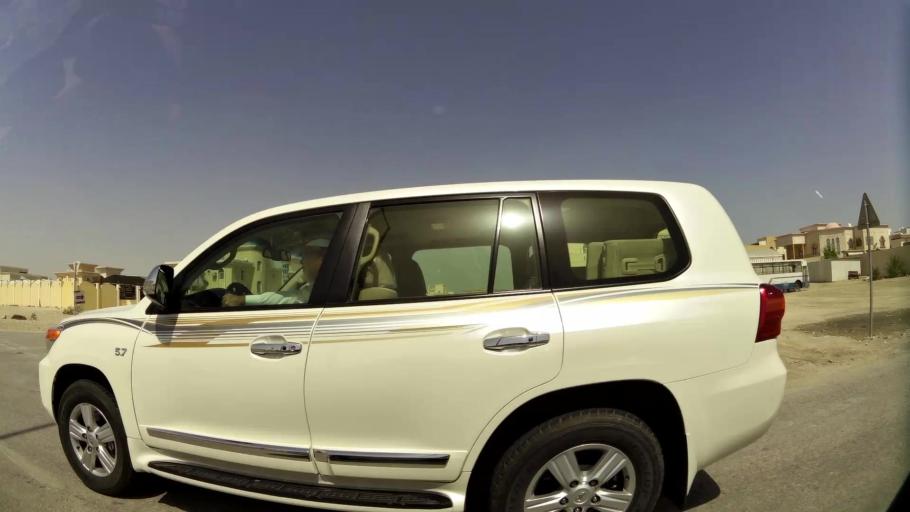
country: QA
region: Baladiyat Umm Salal
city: Umm Salal Muhammad
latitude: 25.3785
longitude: 51.4658
